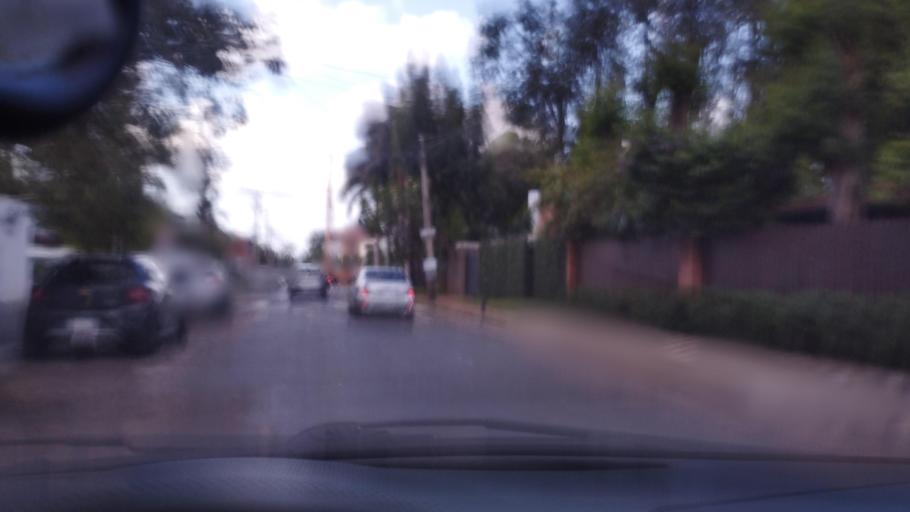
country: PY
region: Central
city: Fernando de la Mora
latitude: -25.3043
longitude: -57.5577
